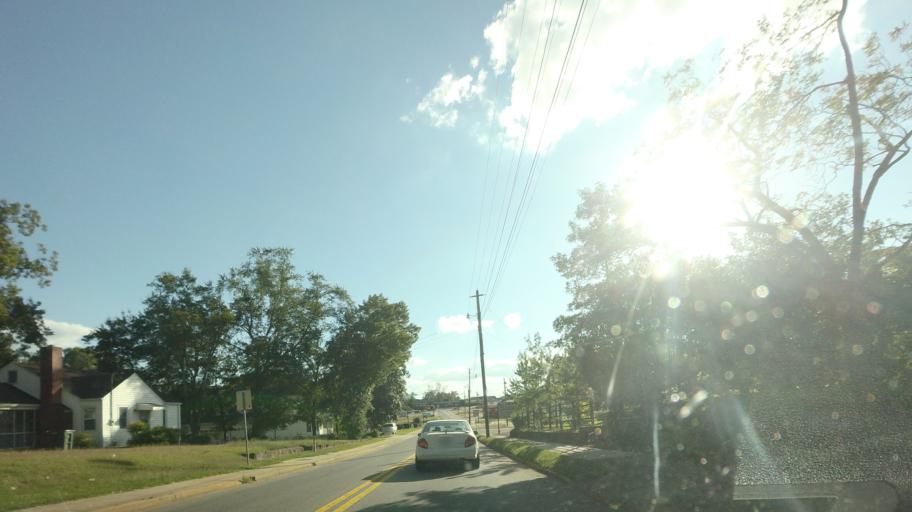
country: US
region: Georgia
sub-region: Upson County
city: Thomaston
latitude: 32.8898
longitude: -84.3212
